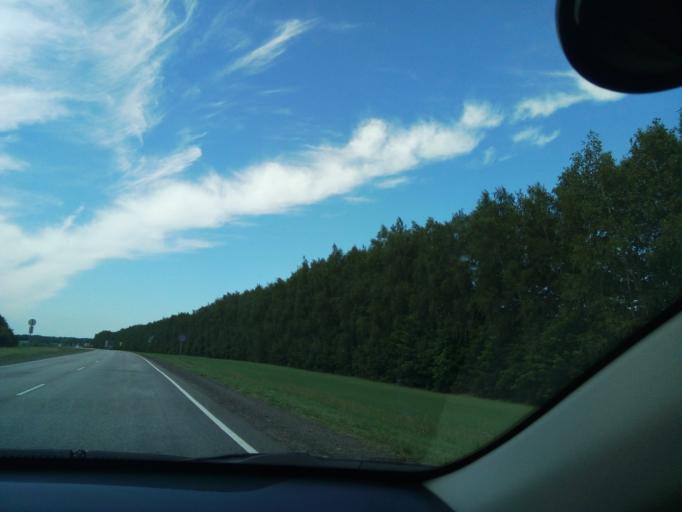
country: RU
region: Tambov
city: Michurinsk
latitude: 52.5874
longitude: 40.3943
